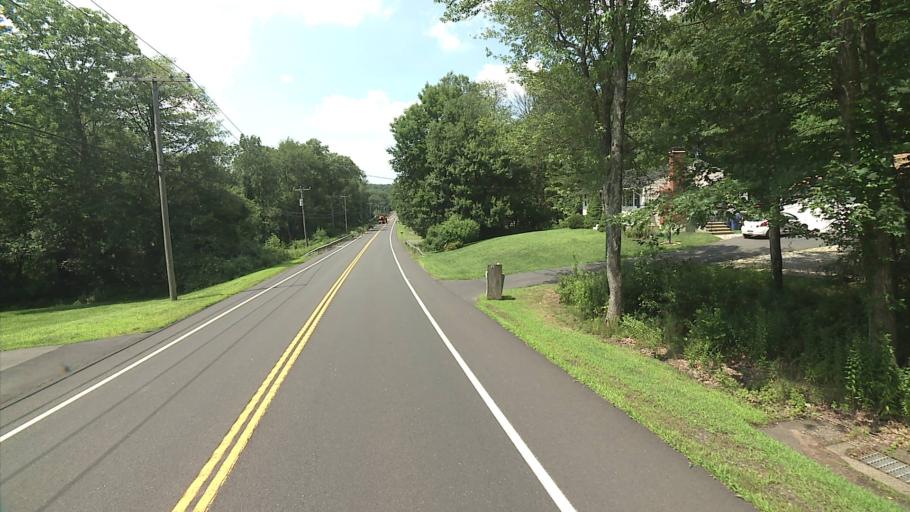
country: US
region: Connecticut
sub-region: Tolland County
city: Tolland
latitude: 41.8324
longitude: -72.4012
